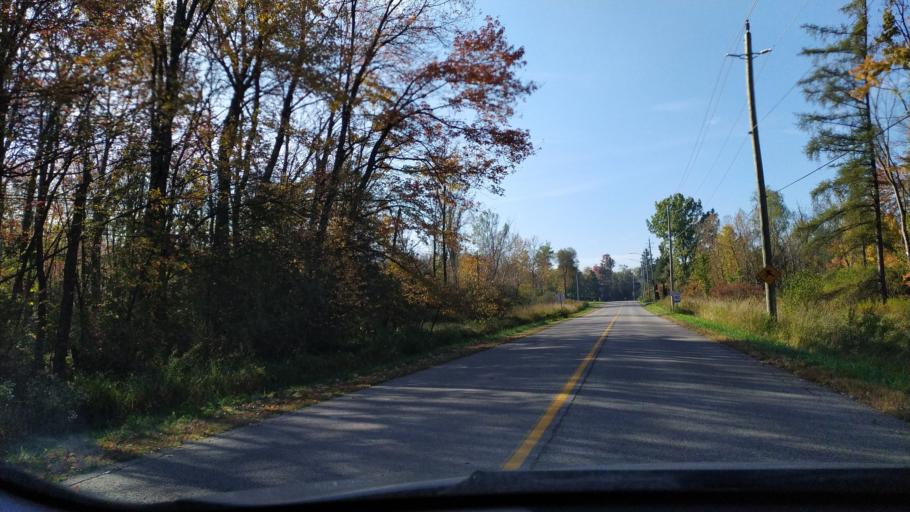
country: CA
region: Ontario
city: Waterloo
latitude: 43.5016
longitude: -80.6557
